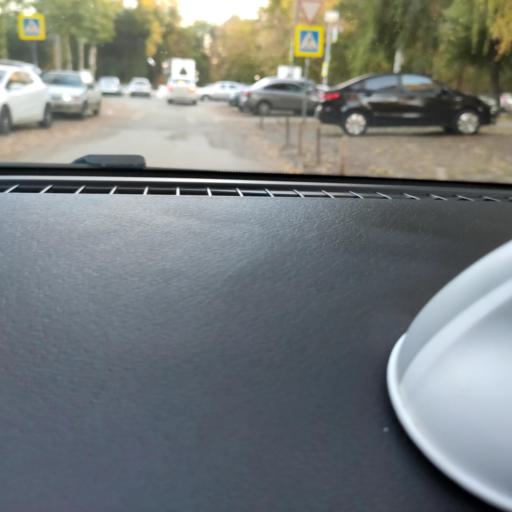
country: RU
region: Samara
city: Samara
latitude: 53.2260
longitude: 50.2404
